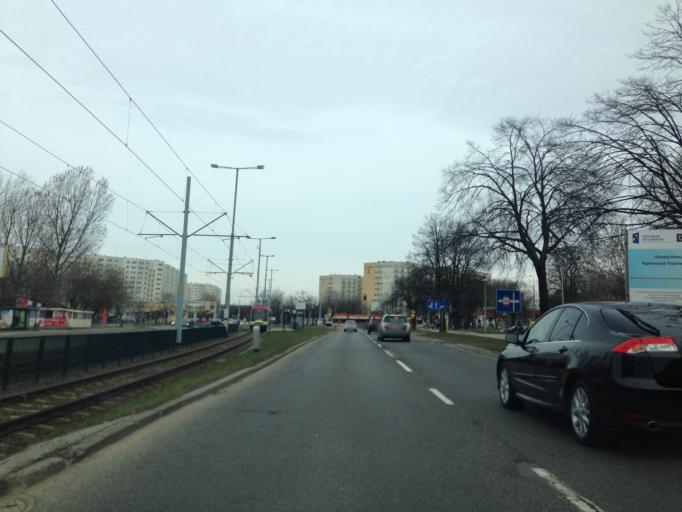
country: PL
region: Pomeranian Voivodeship
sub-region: Sopot
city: Sopot
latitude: 54.4188
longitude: 18.5853
